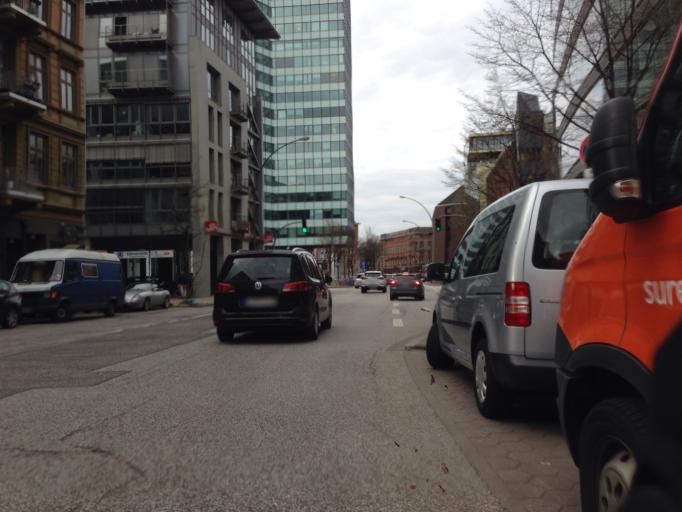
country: DE
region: Hamburg
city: Neustadt
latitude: 53.5550
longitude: 9.9843
